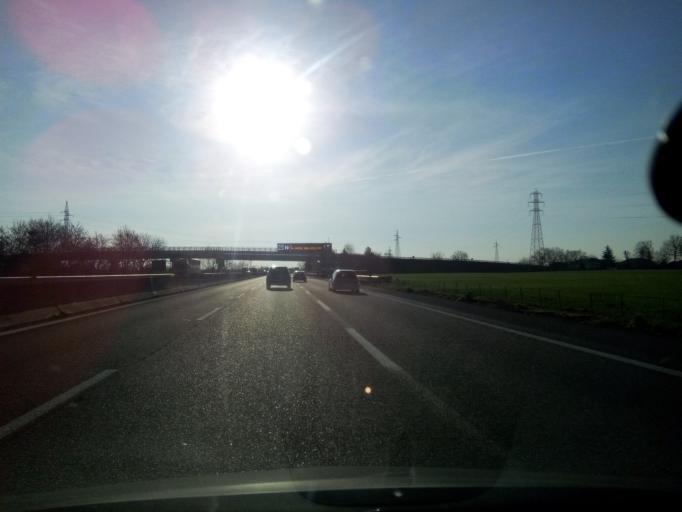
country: IT
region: Emilia-Romagna
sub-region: Provincia di Parma
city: Fontanellato
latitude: 44.8698
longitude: 10.2099
